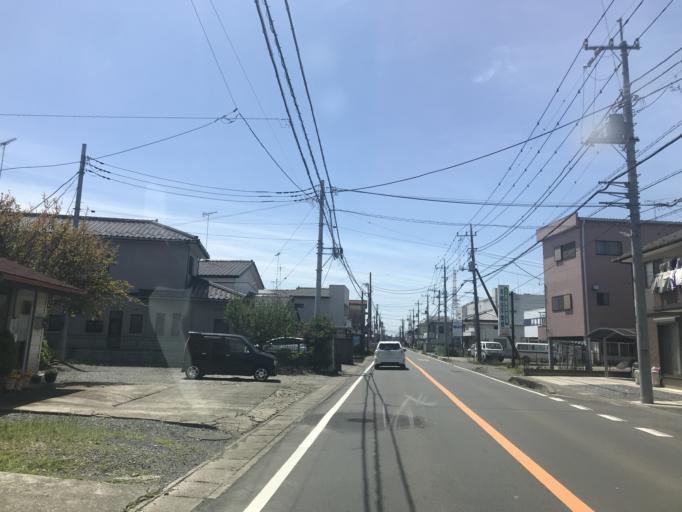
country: JP
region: Ibaraki
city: Shimodate
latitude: 36.2993
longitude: 139.9747
